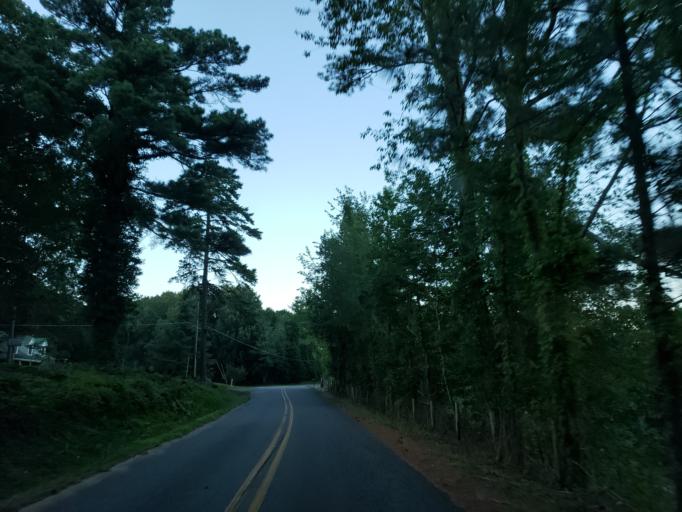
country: US
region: Georgia
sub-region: Bartow County
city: Emerson
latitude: 34.0629
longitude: -84.8290
